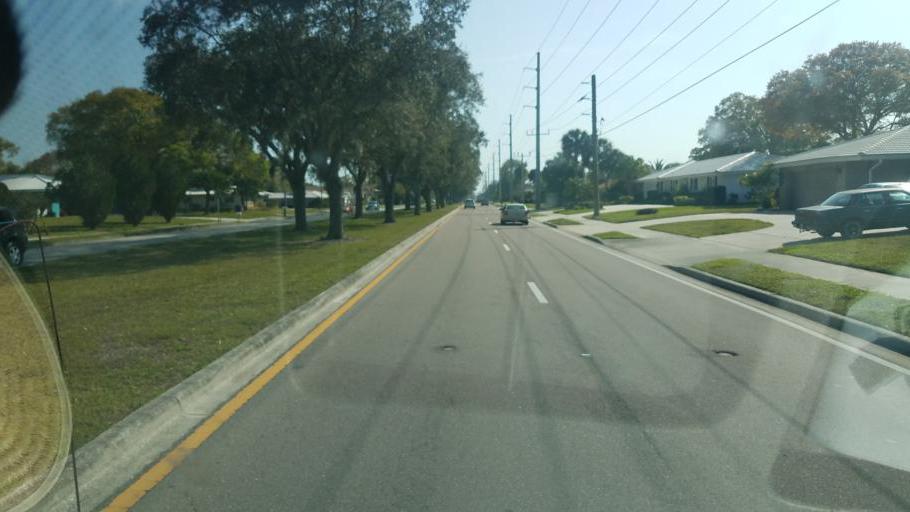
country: US
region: Florida
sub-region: Sarasota County
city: Southgate
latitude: 27.3156
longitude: -82.4976
